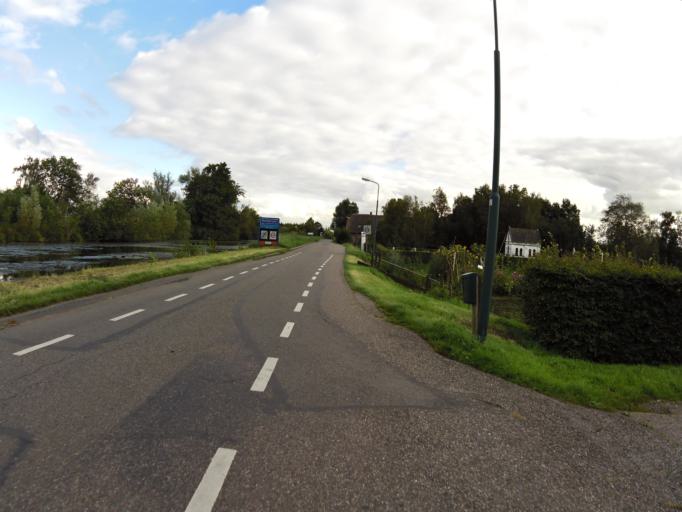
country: NL
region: Utrecht
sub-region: Stichtse Vecht
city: Breukelen
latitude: 52.1456
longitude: 4.9499
